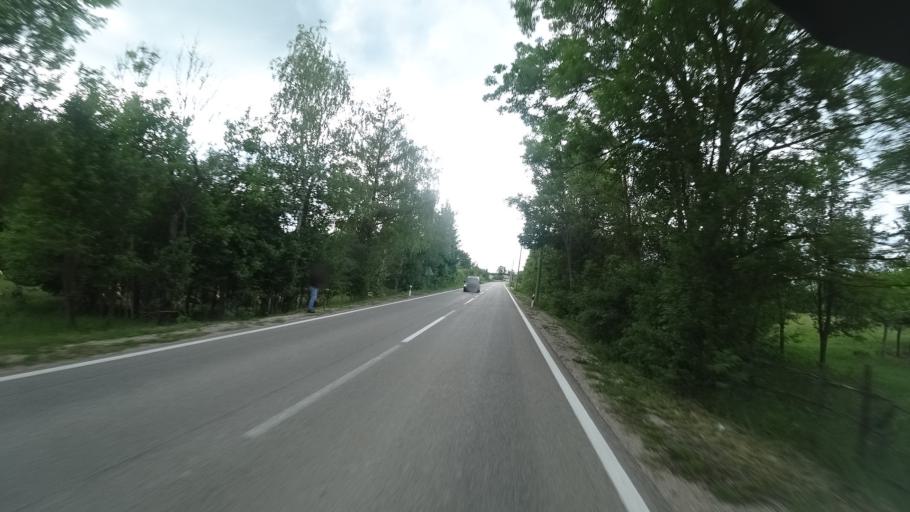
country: HR
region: Licko-Senjska
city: Gospic
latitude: 44.4882
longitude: 15.4640
